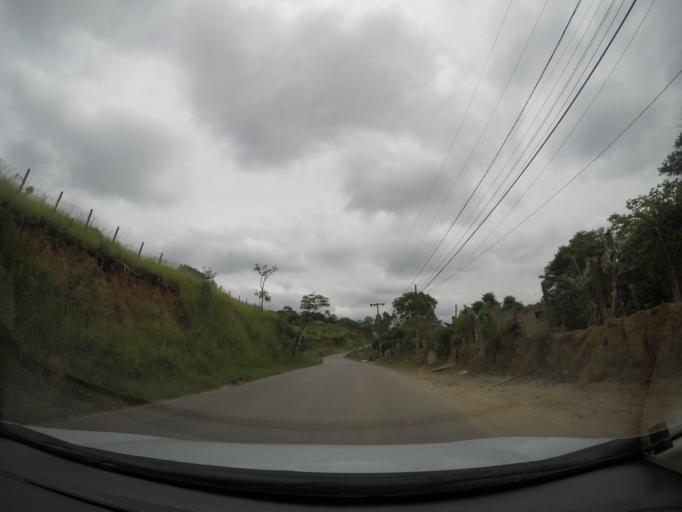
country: BR
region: Sao Paulo
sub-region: Aruja
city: Aruja
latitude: -23.3702
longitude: -46.2960
